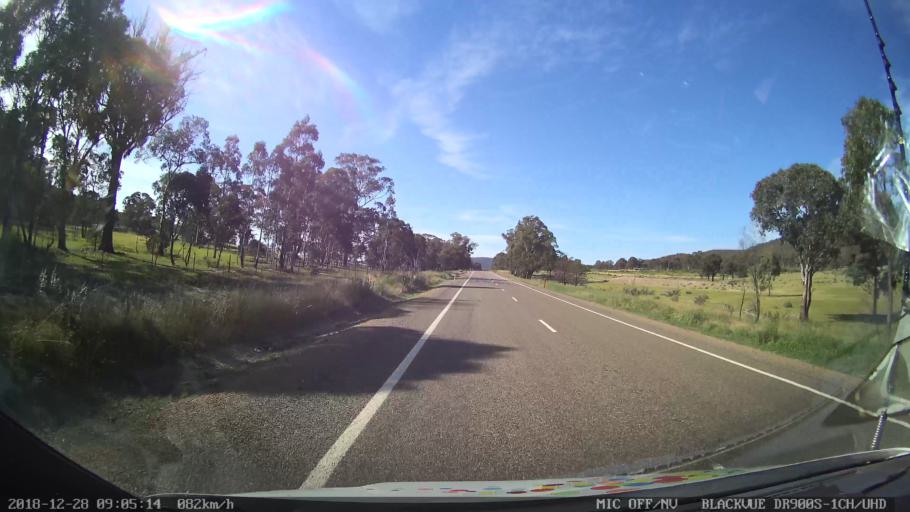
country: AU
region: New South Wales
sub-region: Upper Lachlan Shire
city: Crookwell
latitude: -34.1817
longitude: 149.3476
